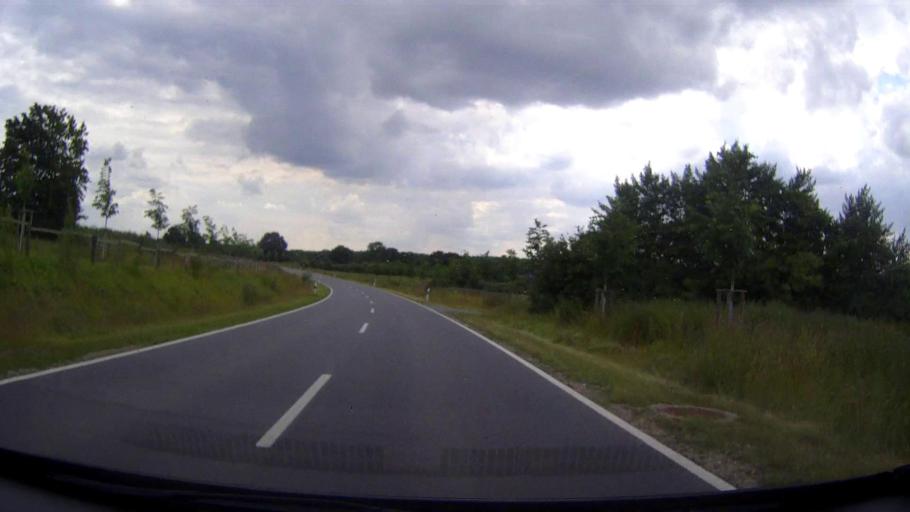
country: DE
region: Schleswig-Holstein
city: Stockelsdorf
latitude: 53.8876
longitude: 10.6065
